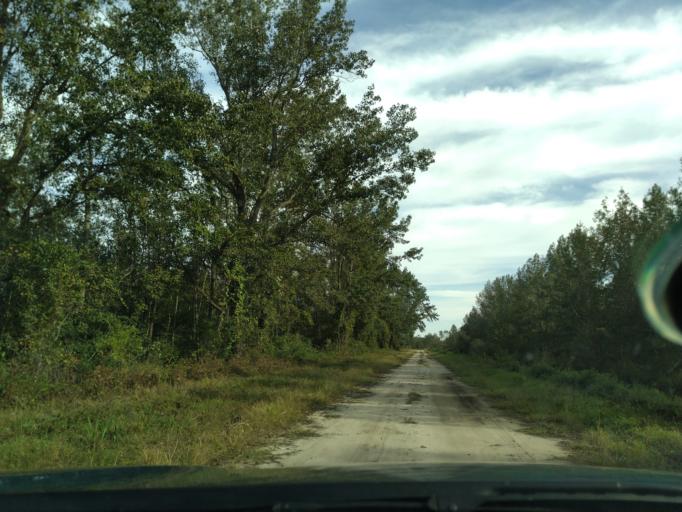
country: US
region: North Carolina
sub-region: Beaufort County
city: Belhaven
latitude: 35.6920
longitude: -76.5532
